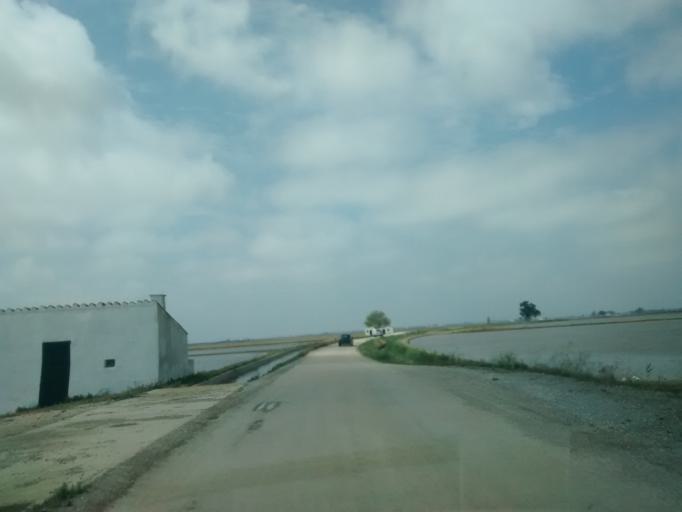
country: ES
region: Catalonia
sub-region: Provincia de Tarragona
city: Deltebre
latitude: 40.6837
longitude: 0.7911
